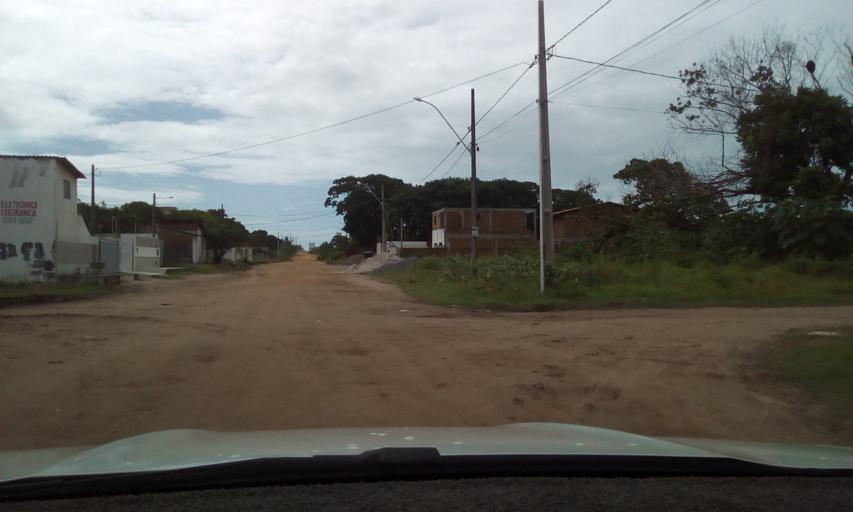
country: BR
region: Paraiba
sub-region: Joao Pessoa
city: Joao Pessoa
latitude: -7.1483
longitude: -34.8157
